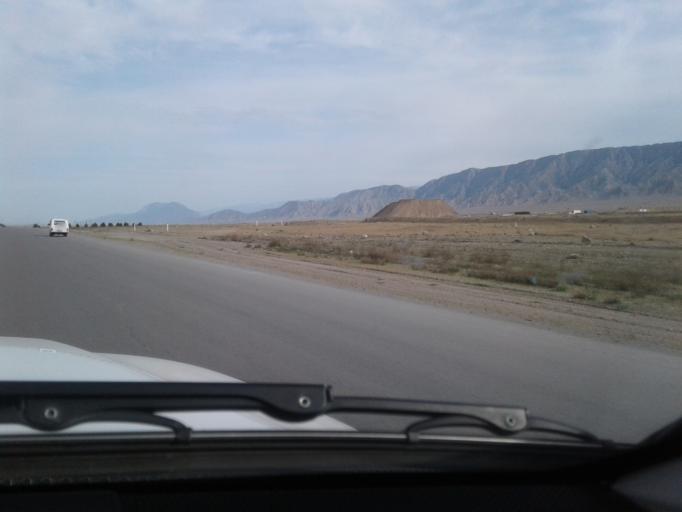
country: TM
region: Ahal
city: Arcabil
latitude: 38.2227
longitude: 57.7981
